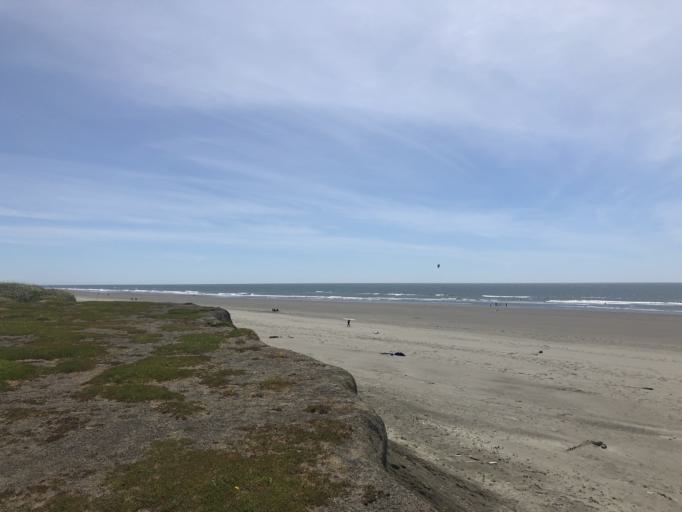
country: US
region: Washington
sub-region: Grays Harbor County
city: Westport
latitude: 46.9039
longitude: -124.1322
